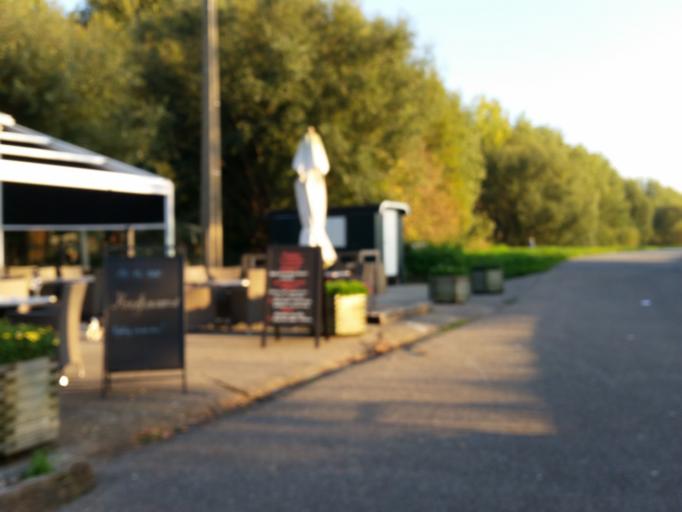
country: BE
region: Flanders
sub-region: Provincie Antwerpen
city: Niel
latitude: 51.1182
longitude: 4.3128
